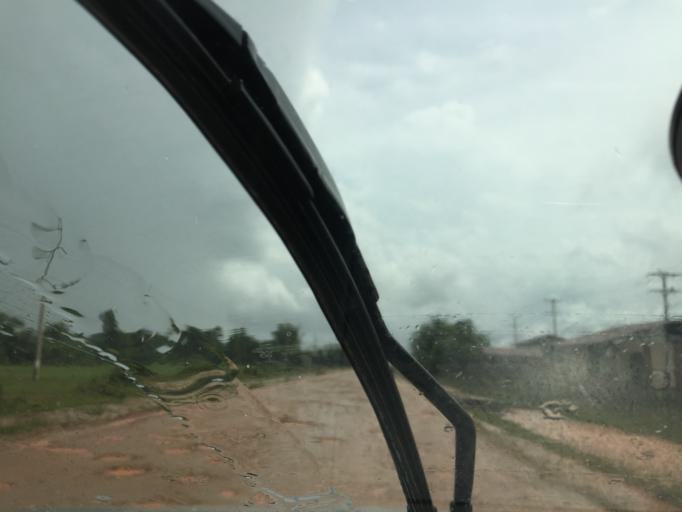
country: LA
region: Attapu
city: Attapu
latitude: 14.8196
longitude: 106.7934
